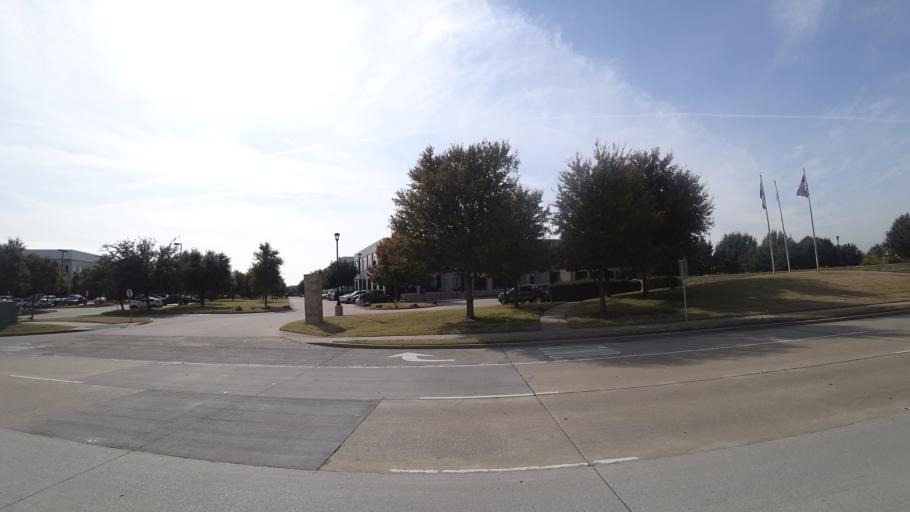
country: US
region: Texas
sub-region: Denton County
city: The Colony
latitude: 33.0702
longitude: -96.8725
